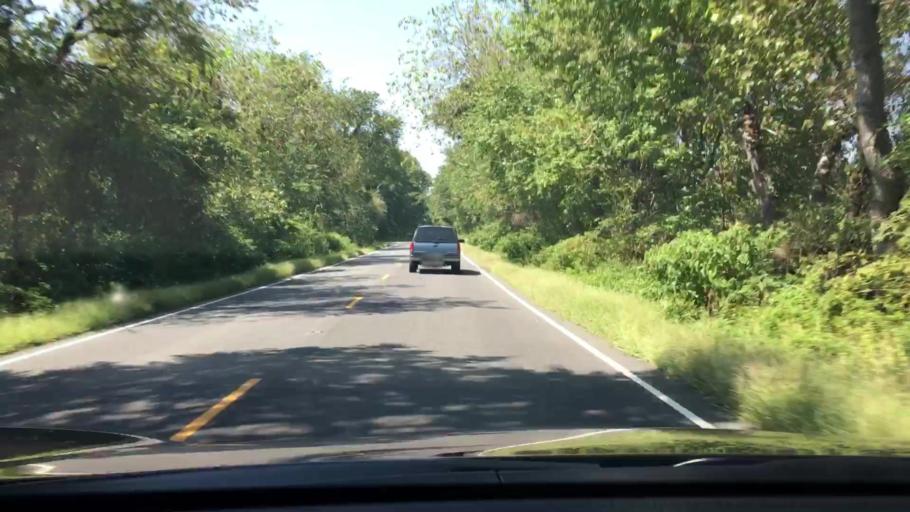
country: US
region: New Jersey
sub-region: Cape May County
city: Woodbine
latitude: 39.2607
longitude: -74.8995
